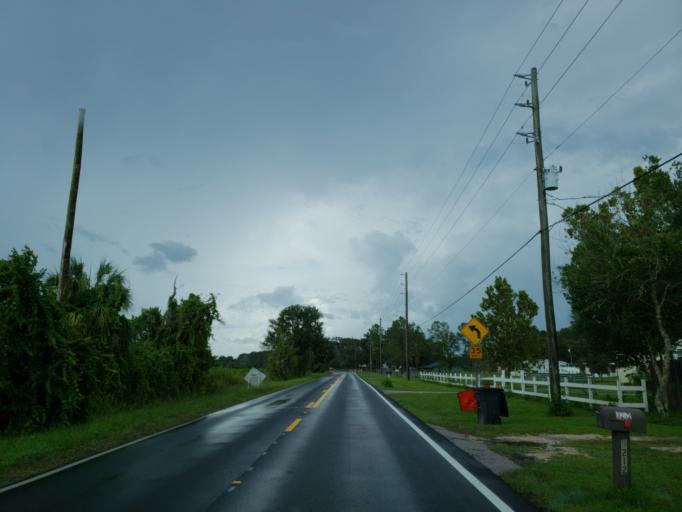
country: US
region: Florida
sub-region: Pasco County
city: Land O' Lakes
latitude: 28.2917
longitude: -82.4328
